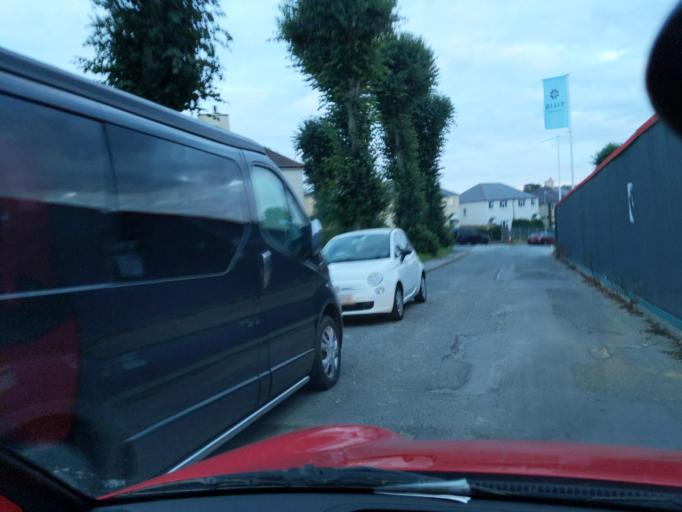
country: GB
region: England
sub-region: Cornwall
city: Millbrook
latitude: 50.3910
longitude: -4.1672
